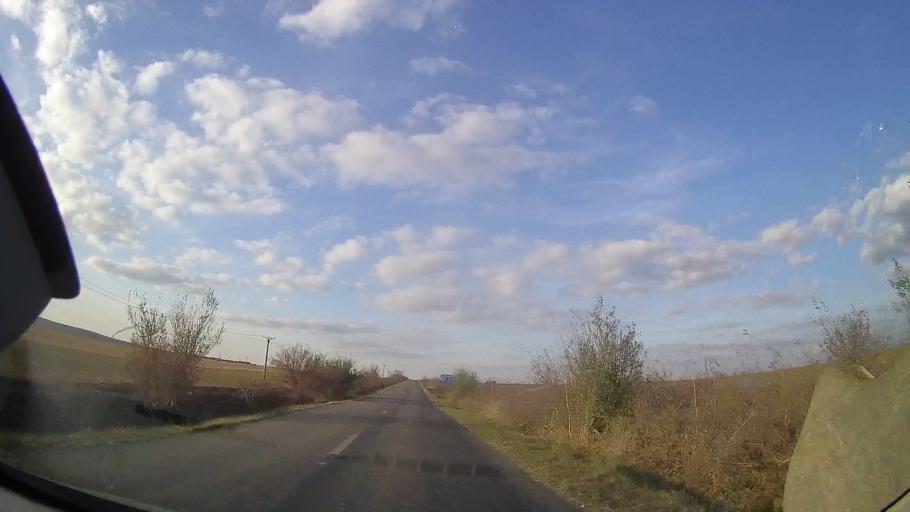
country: RO
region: Constanta
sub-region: Comuna Dumbraveni
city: Dumbraveni
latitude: 43.9304
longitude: 28.0278
